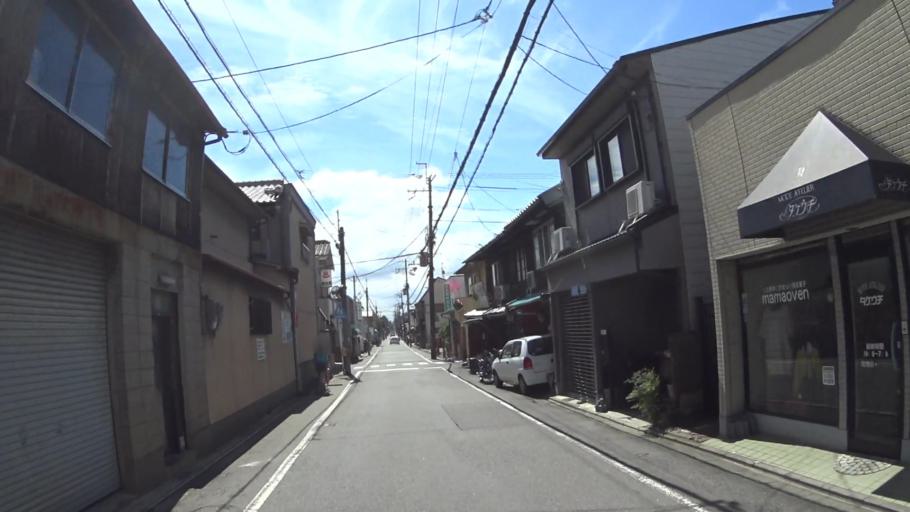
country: JP
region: Kyoto
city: Muko
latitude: 34.9530
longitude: 135.7679
